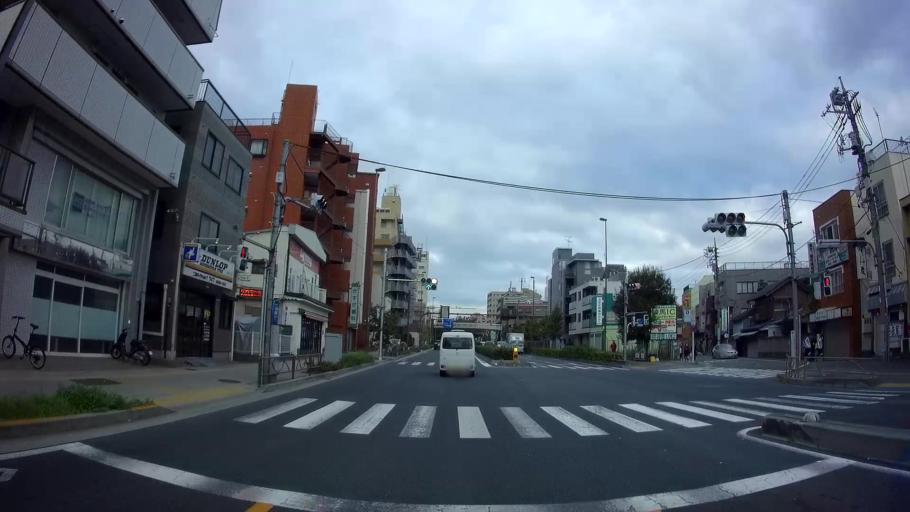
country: JP
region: Saitama
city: Shimotoda
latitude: 35.7601
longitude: 139.6781
